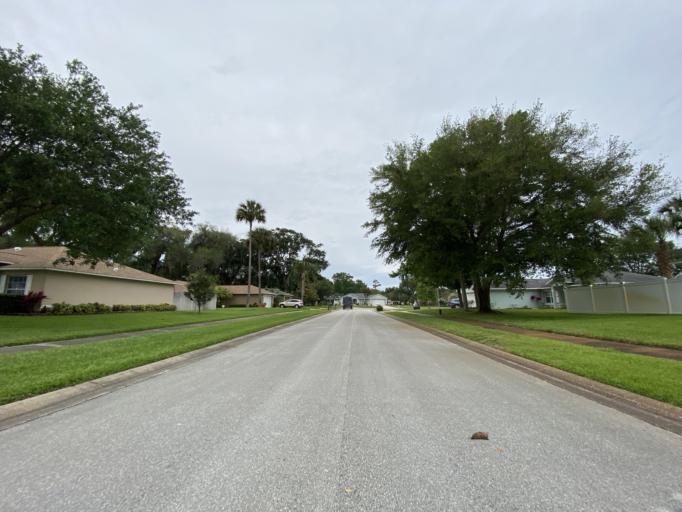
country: US
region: Florida
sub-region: Volusia County
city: Port Orange
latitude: 29.1511
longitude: -81.0022
